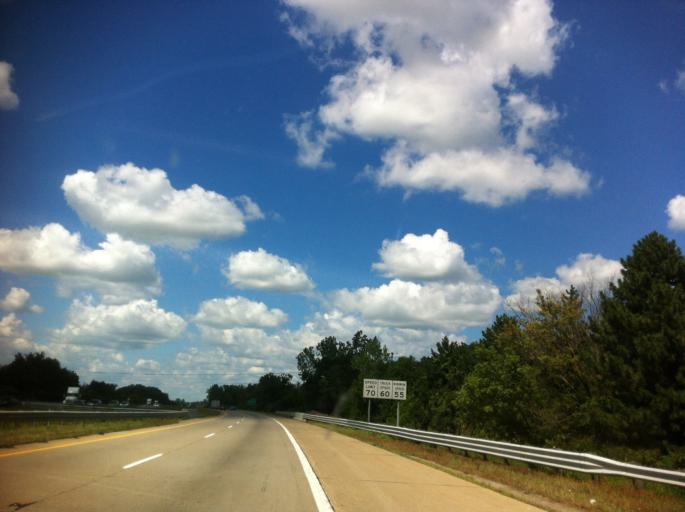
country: US
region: Ohio
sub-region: Lucas County
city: Sylvania
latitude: 41.7318
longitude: -83.6893
